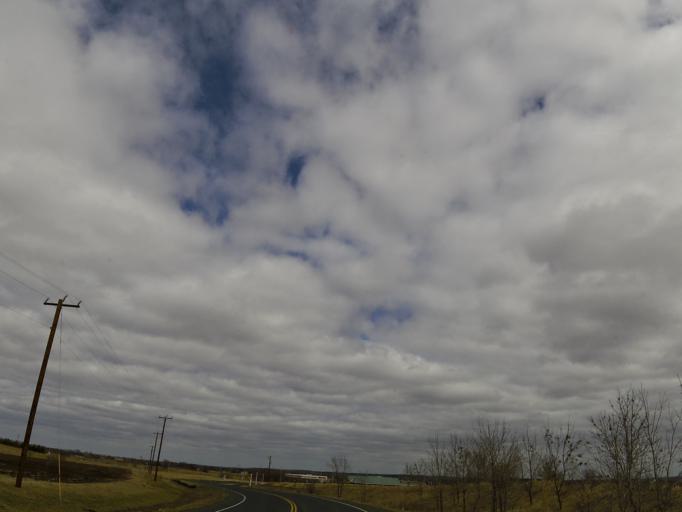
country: US
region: Minnesota
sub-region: Washington County
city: Lake Elmo
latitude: 44.9494
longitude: -92.9072
